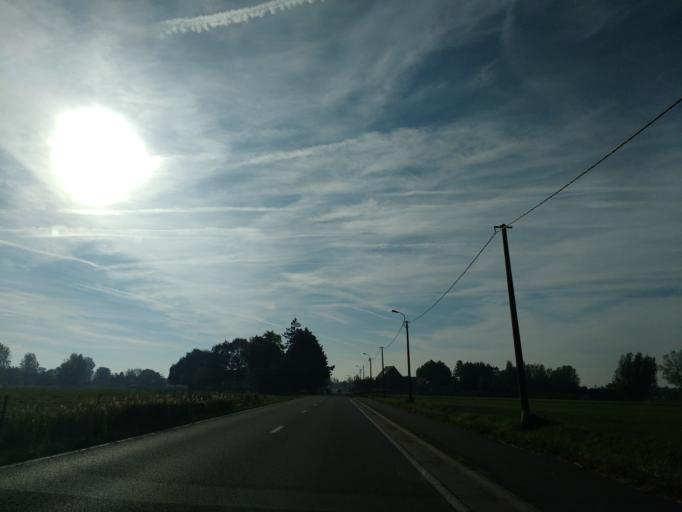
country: BE
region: Flanders
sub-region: Provincie Oost-Vlaanderen
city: Kaprijke
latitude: 51.2542
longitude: 3.6137
